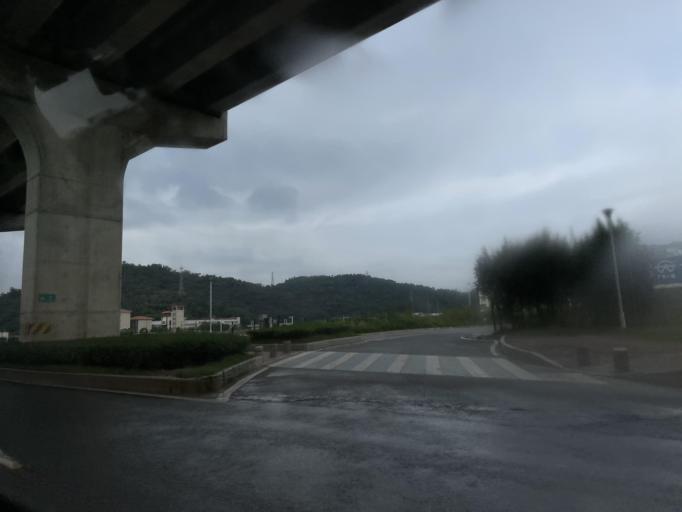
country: CN
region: Guangdong
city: Wanzai
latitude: 22.1765
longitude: 113.4865
